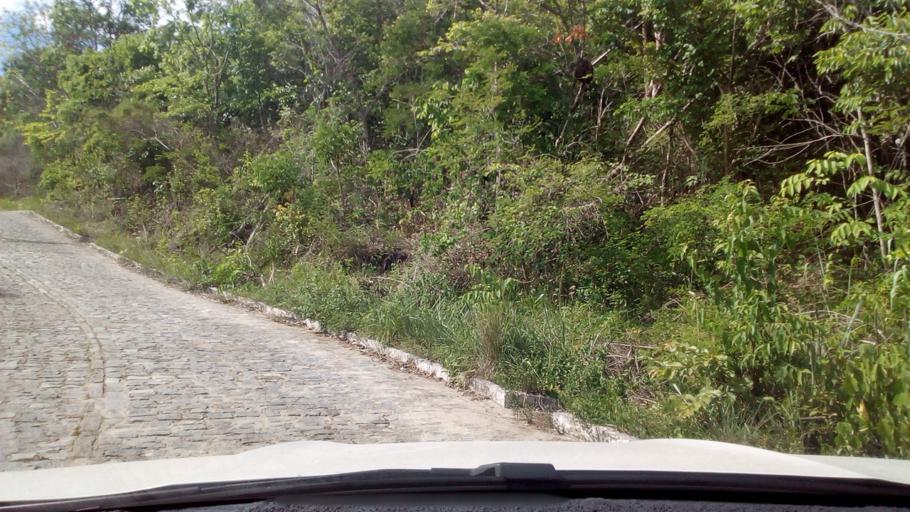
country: BR
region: Paraiba
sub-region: Guarabira
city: Guarabira
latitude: -6.8333
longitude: -35.4952
